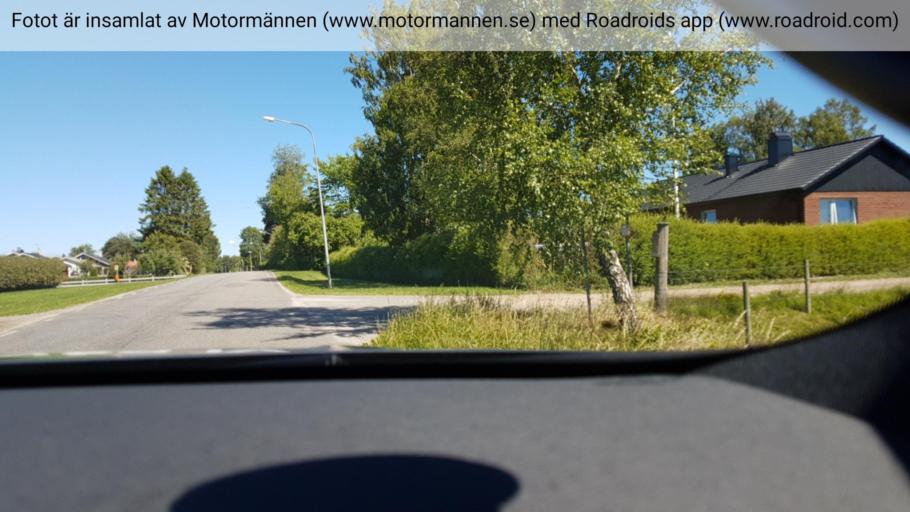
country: SE
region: Vaestra Goetaland
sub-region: Falkopings Kommun
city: Falkoeping
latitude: 58.0717
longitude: 13.5139
